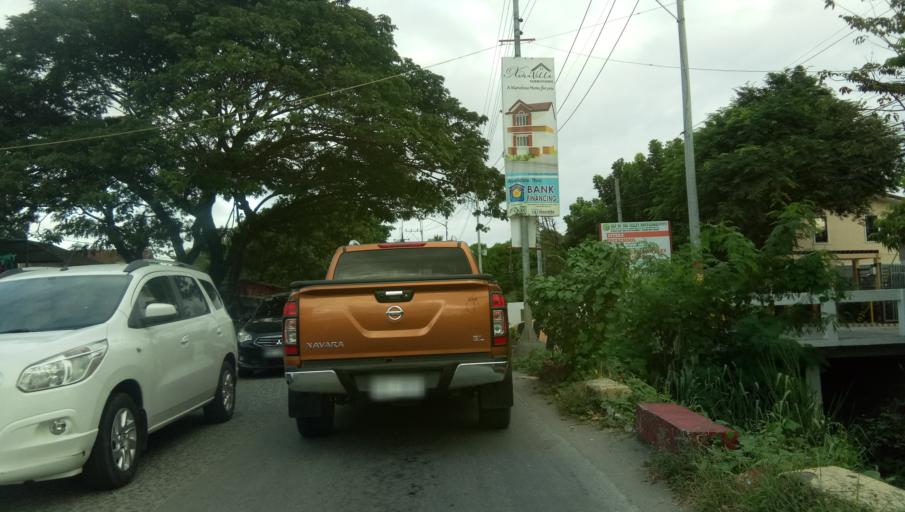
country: PH
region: Calabarzon
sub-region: Province of Cavite
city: Dasmarinas
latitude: 14.3677
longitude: 120.9255
